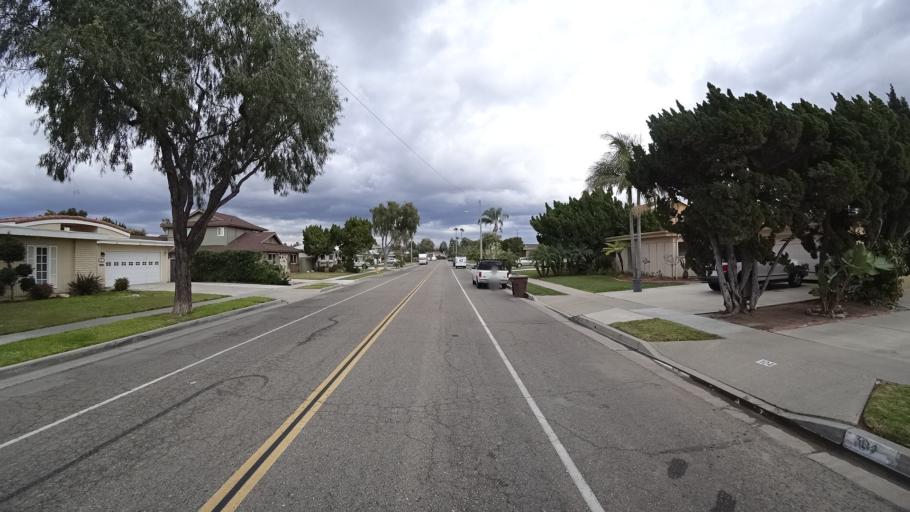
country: US
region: California
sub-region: Orange County
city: Placentia
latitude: 33.8409
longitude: -117.8637
